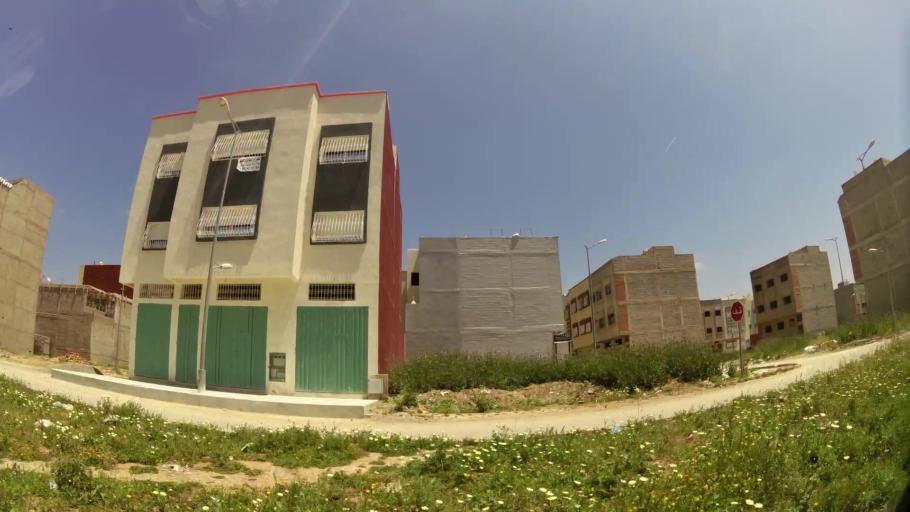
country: MA
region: Fes-Boulemane
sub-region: Fes
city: Fes
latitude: 34.0327
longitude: -5.0548
